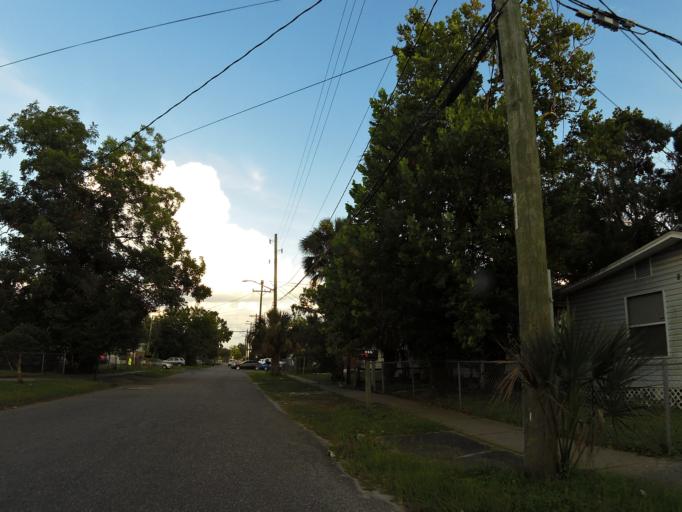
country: US
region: Florida
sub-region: Duval County
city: Jacksonville
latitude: 30.3362
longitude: -81.6920
